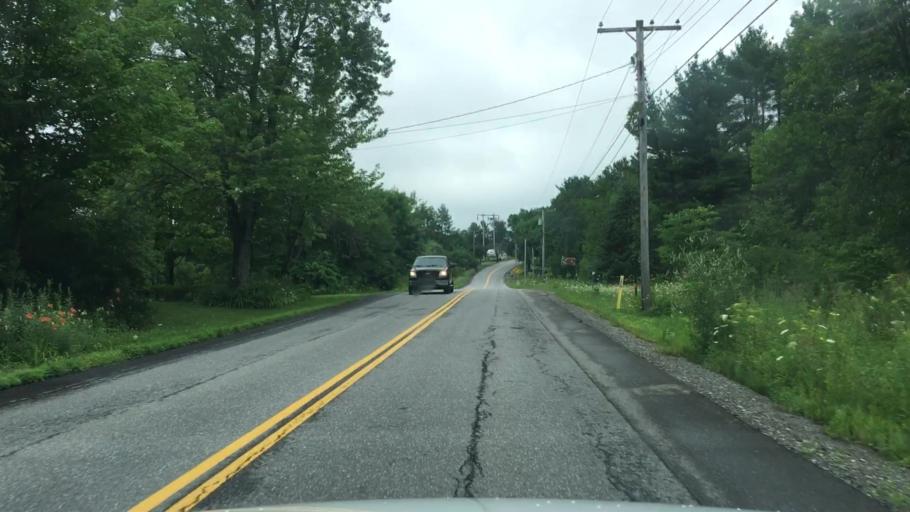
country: US
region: Maine
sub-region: Kennebec County
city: Augusta
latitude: 44.3234
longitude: -69.7335
